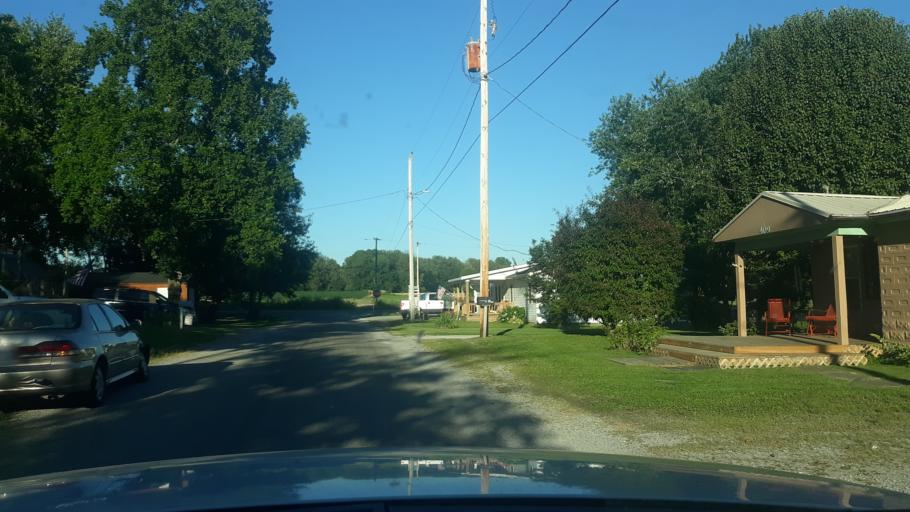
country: US
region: Illinois
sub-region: Saline County
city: Harrisburg
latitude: 37.8432
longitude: -88.6063
